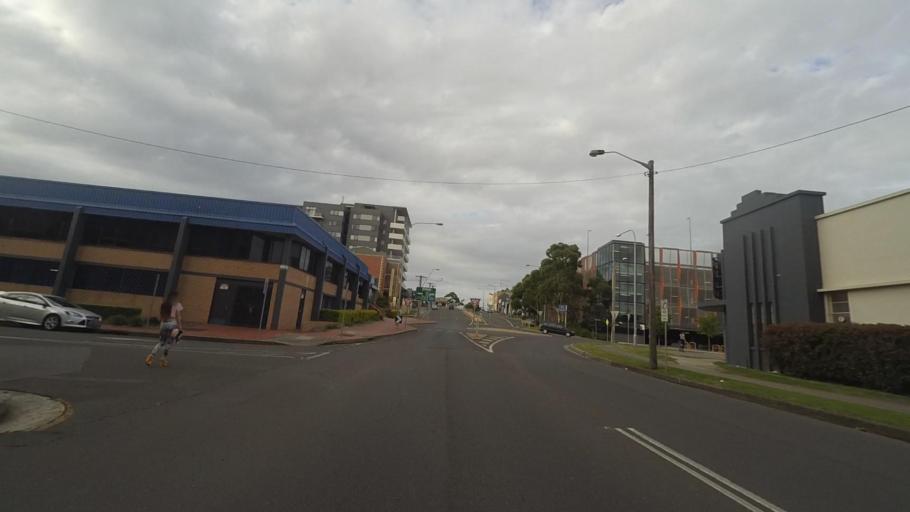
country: AU
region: New South Wales
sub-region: Wollongong
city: Wollongong
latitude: -34.4278
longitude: 150.8869
